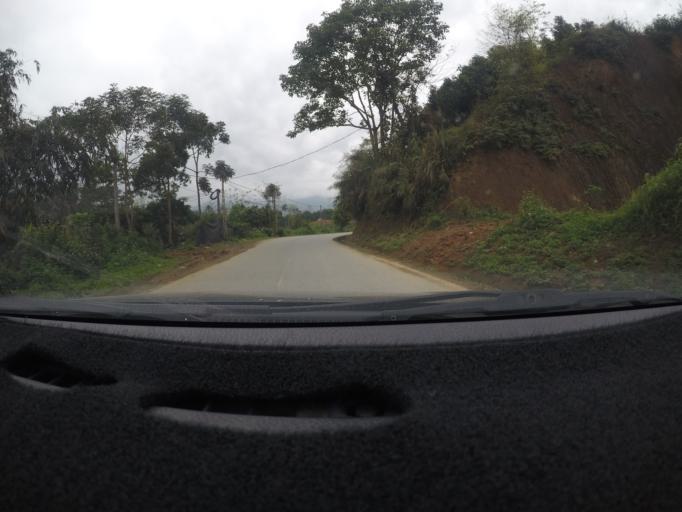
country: VN
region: Yen Bai
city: Co Phuc
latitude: 21.9262
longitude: 104.7963
